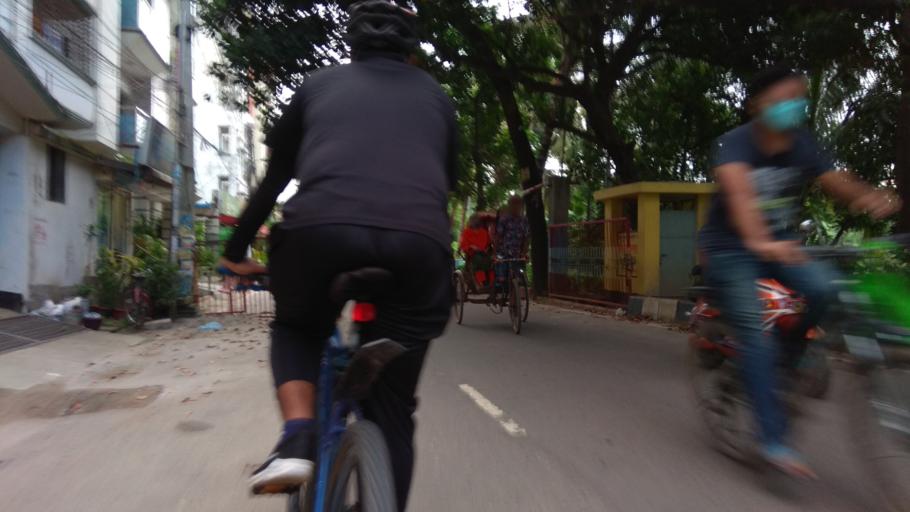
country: BD
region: Dhaka
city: Tungi
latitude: 23.8686
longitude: 90.3922
